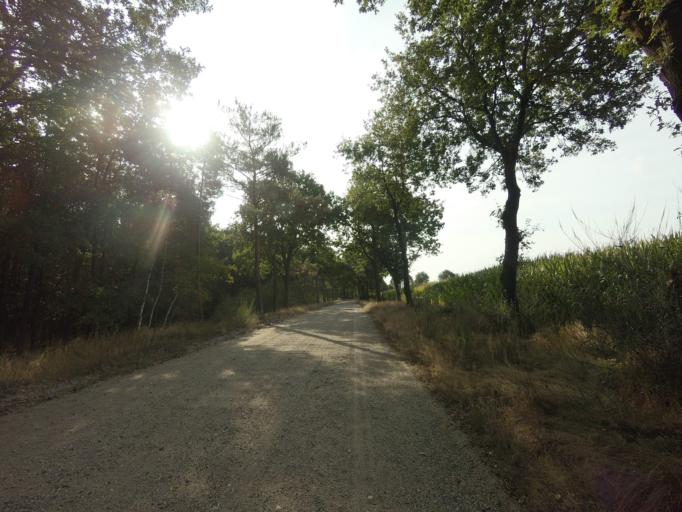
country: NL
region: North Brabant
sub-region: Gemeente Mill en Sint Hubert
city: Wilbertoord
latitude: 51.6581
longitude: 5.7845
